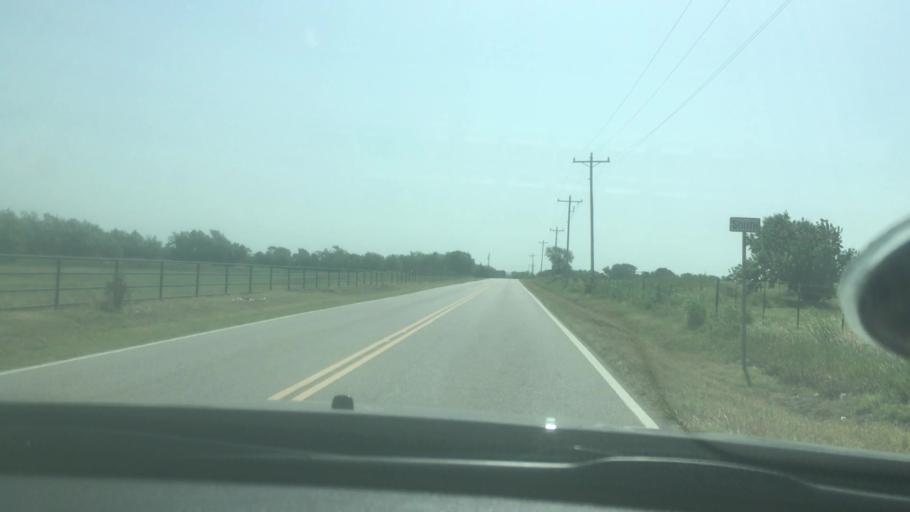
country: US
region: Oklahoma
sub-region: Bryan County
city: Durant
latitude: 34.0847
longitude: -96.4156
